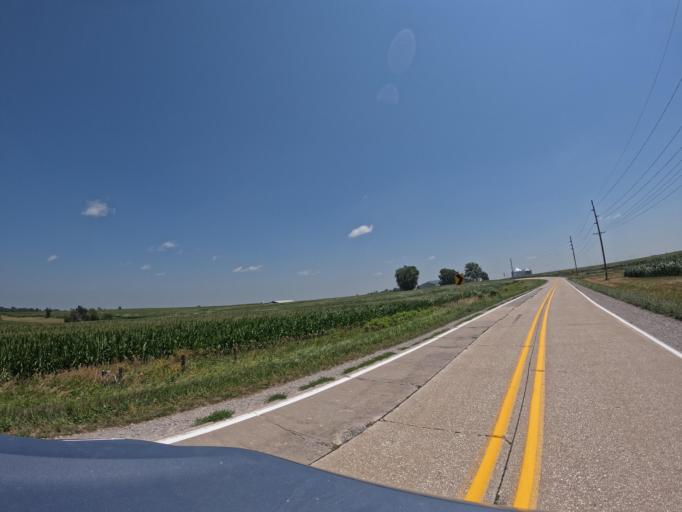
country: US
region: Iowa
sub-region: Keokuk County
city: Sigourney
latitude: 41.2754
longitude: -92.1601
